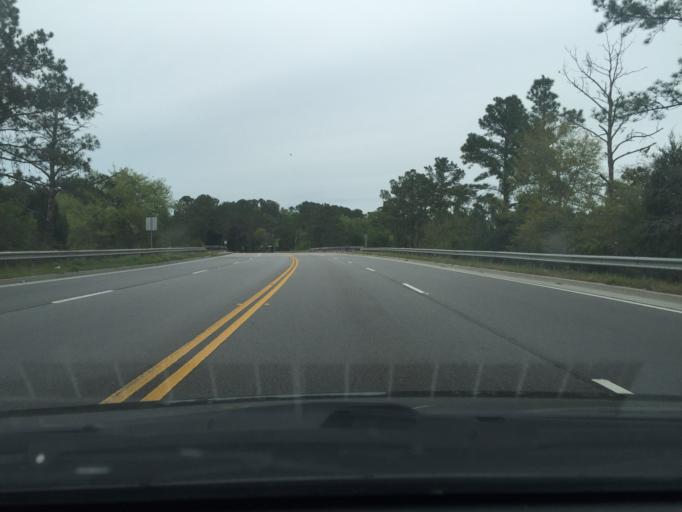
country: US
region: Georgia
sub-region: Chatham County
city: Isle of Hope
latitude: 31.9873
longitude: -81.1049
